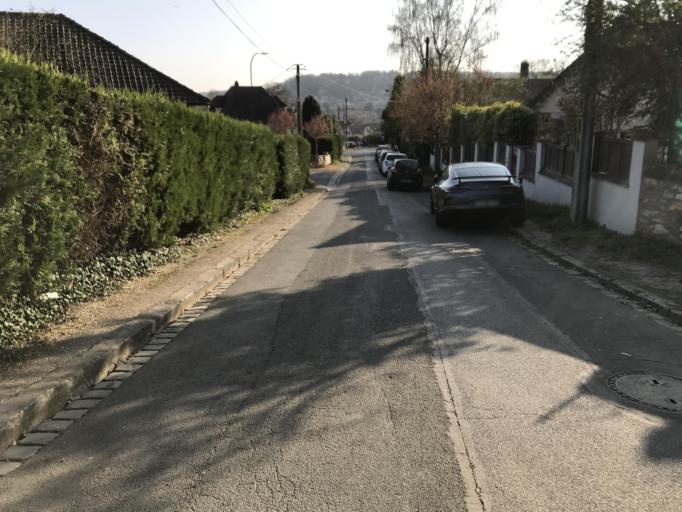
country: FR
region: Ile-de-France
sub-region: Departement de l'Essonne
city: Bures-sur-Yvette
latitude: 48.7035
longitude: 2.1549
